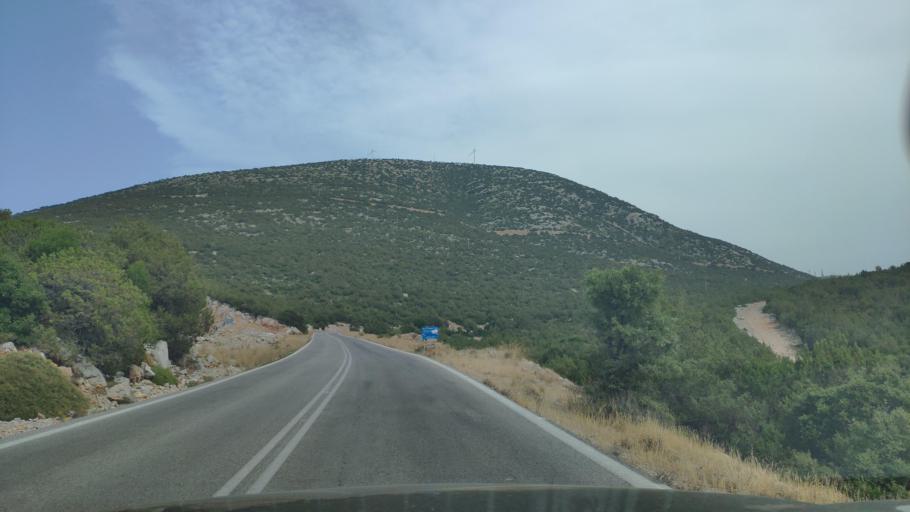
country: GR
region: Peloponnese
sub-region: Nomos Argolidos
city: Didyma
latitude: 37.5047
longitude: 23.1898
